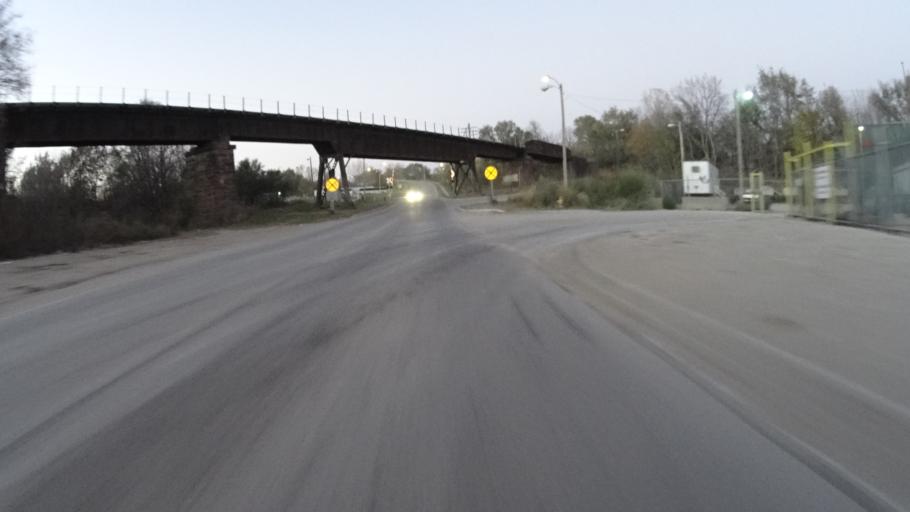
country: US
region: Nebraska
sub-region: Douglas County
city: Omaha
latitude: 41.2222
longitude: -95.9596
